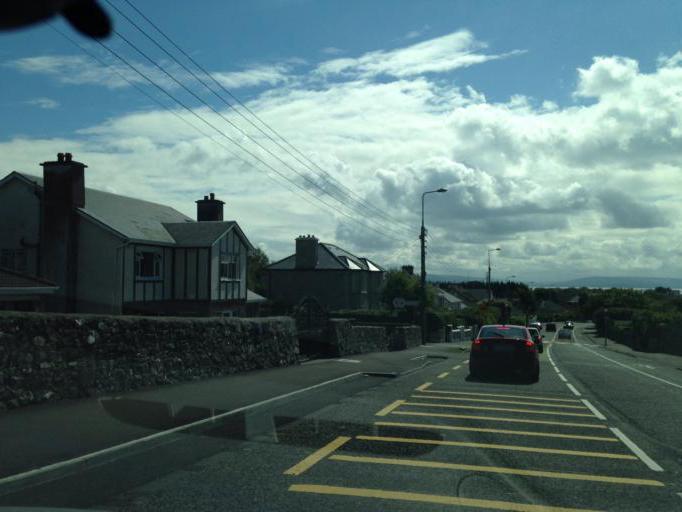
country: IE
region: Connaught
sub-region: County Galway
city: Gaillimh
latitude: 53.2664
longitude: -9.0881
